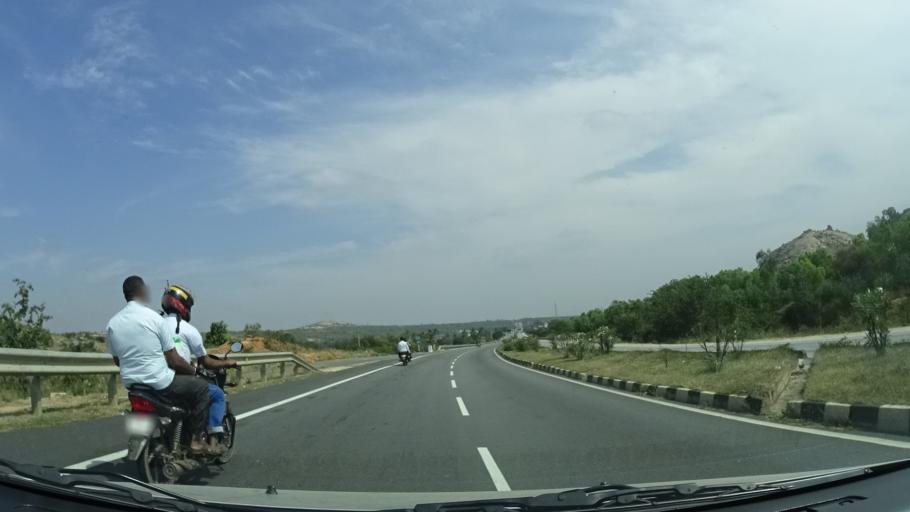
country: IN
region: Karnataka
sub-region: Chikkaballapur
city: Chik Ballapur
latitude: 13.5325
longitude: 77.7657
